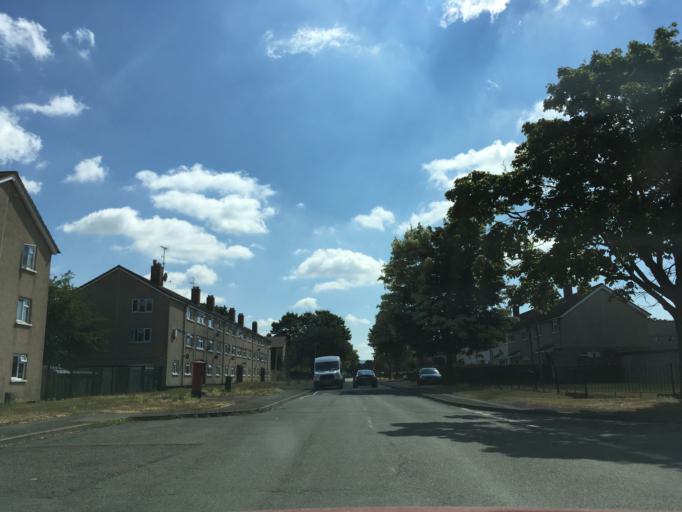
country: GB
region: England
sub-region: Gloucestershire
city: Uckington
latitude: 51.9041
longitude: -2.1195
